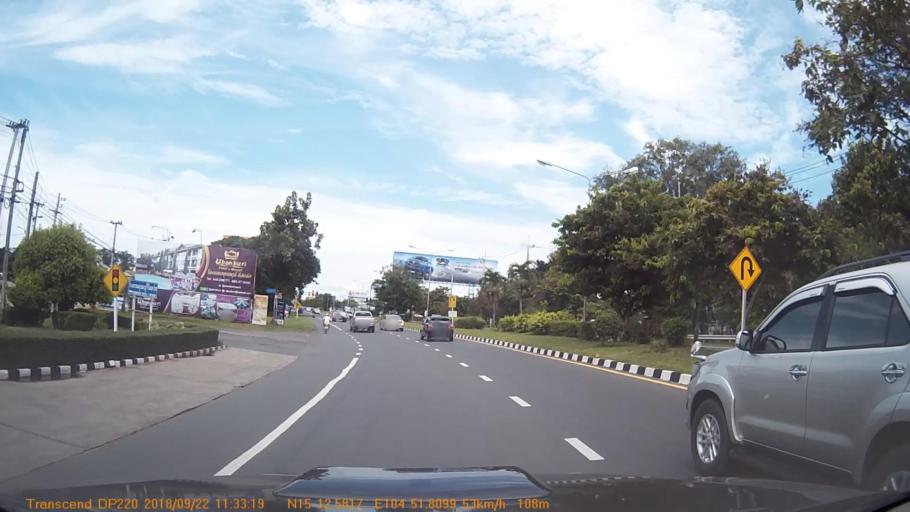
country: TH
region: Changwat Ubon Ratchathani
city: Warin Chamrap
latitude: 15.2096
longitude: 104.8636
